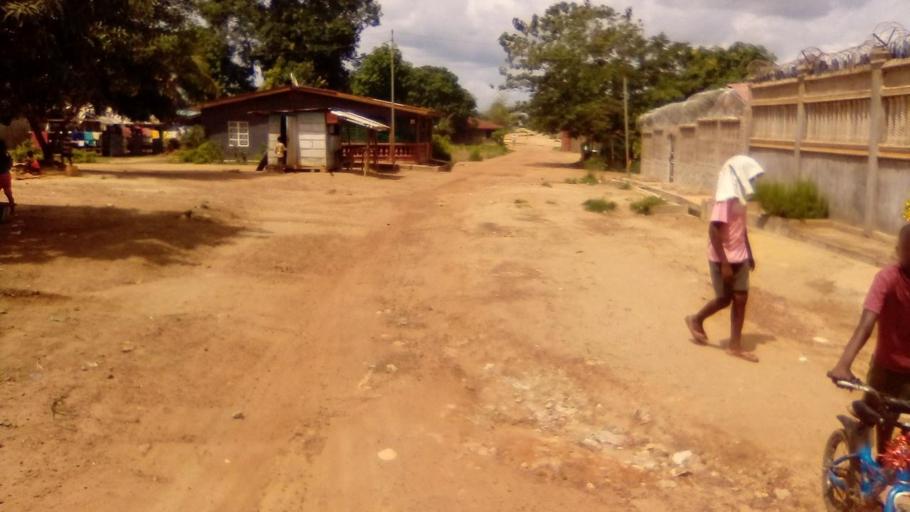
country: SL
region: Southern Province
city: Bo
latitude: 7.9671
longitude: -11.7249
